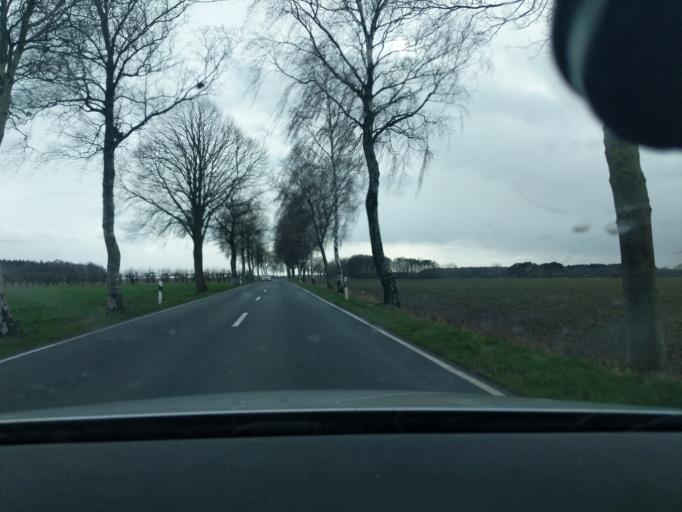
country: DE
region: Lower Saxony
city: Bliedersdorf
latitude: 53.5002
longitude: 9.5385
